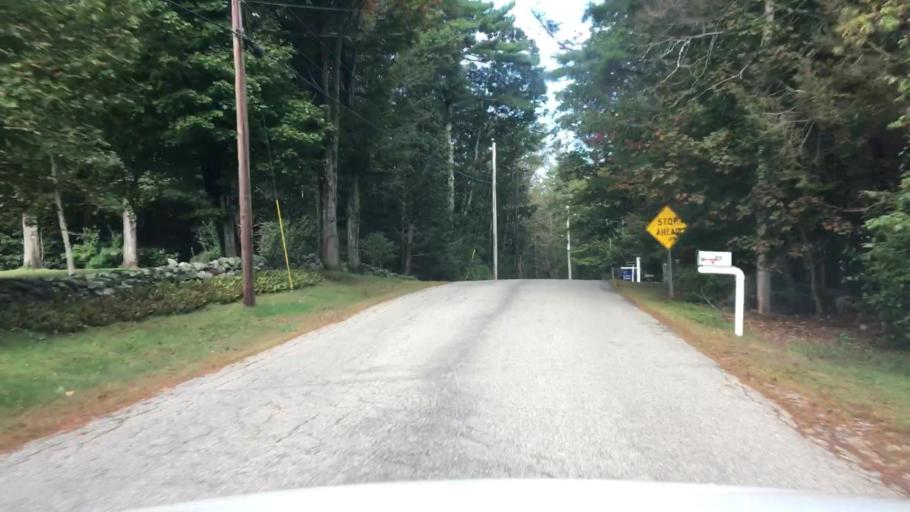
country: US
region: Maine
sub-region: York County
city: York Harbor
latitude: 43.1188
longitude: -70.6784
